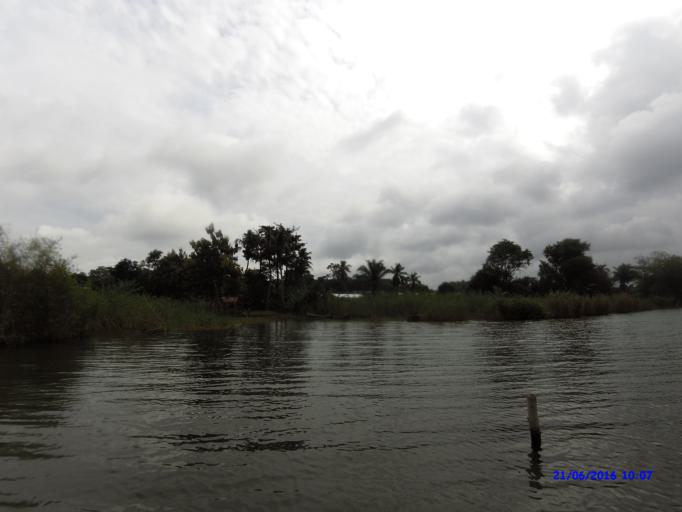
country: BJ
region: Mono
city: Come
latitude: 6.4592
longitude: 1.9267
